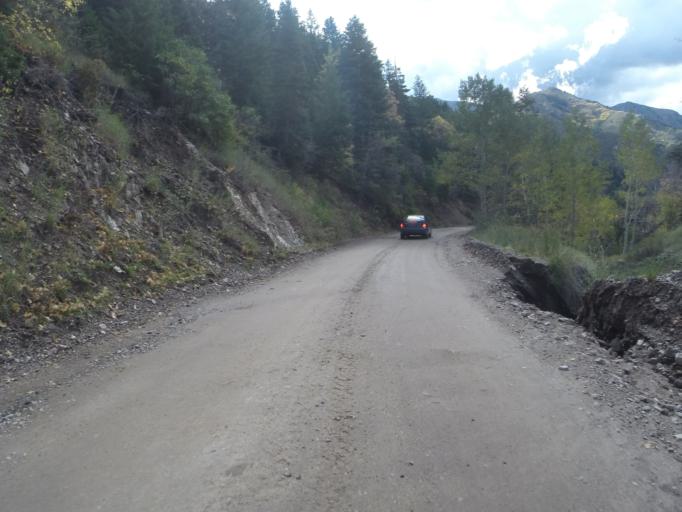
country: US
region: Utah
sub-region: Tooele County
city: Tooele
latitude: 40.4849
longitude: -112.1817
